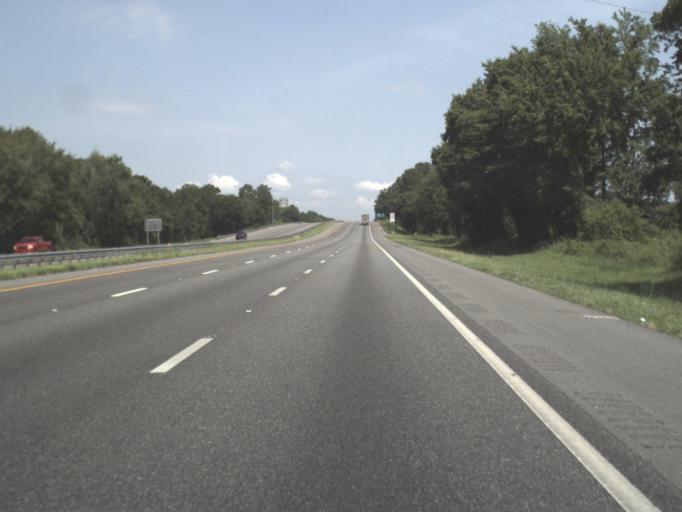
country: US
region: Florida
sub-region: Hamilton County
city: Jasper
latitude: 30.4540
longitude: -82.9415
